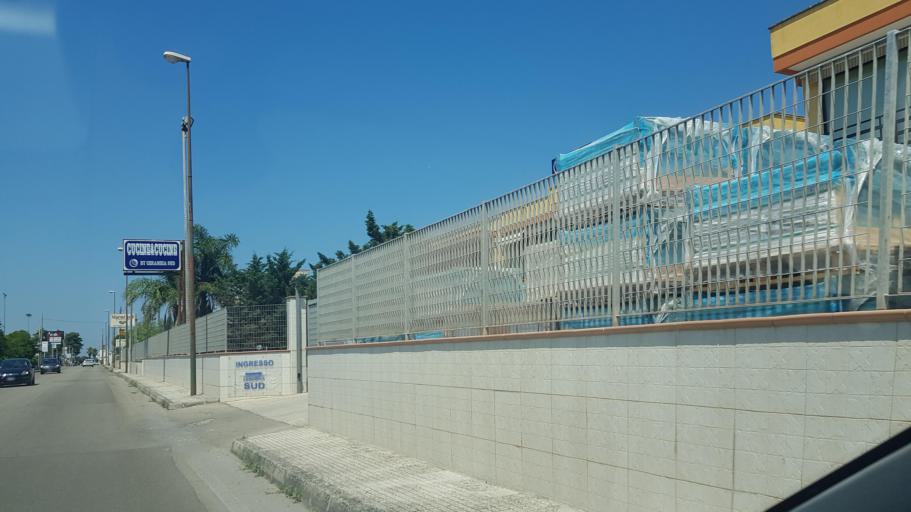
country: IT
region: Apulia
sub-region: Provincia di Lecce
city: Melendugno
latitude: 40.2751
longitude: 18.3442
